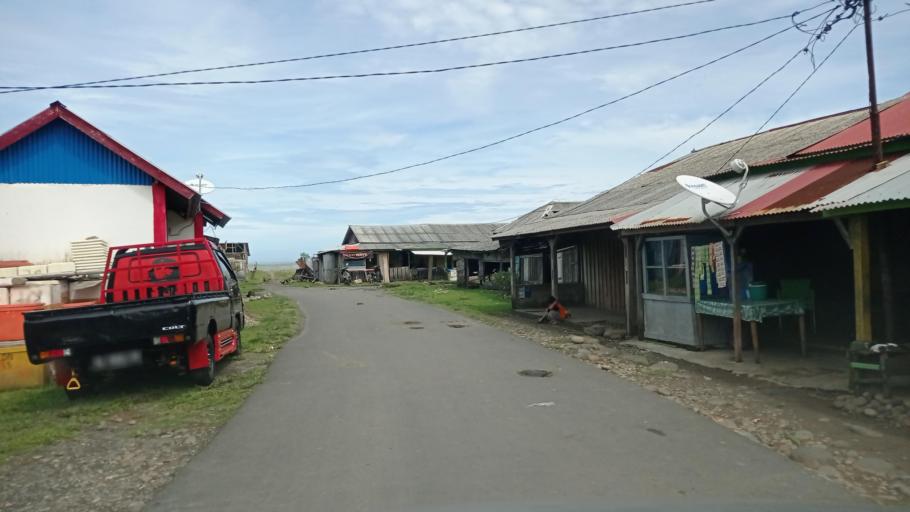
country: ID
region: Bengkulu
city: Ipuh
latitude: -2.5876
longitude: 101.1130
